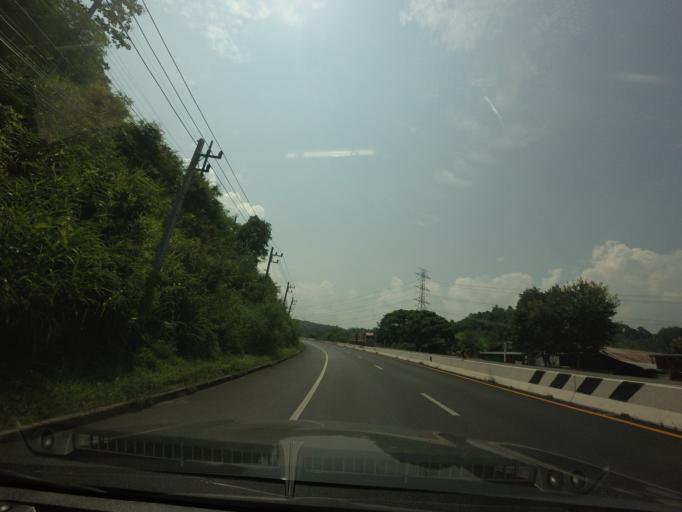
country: TH
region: Phrae
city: Den Chai
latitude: 17.8922
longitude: 100.0484
